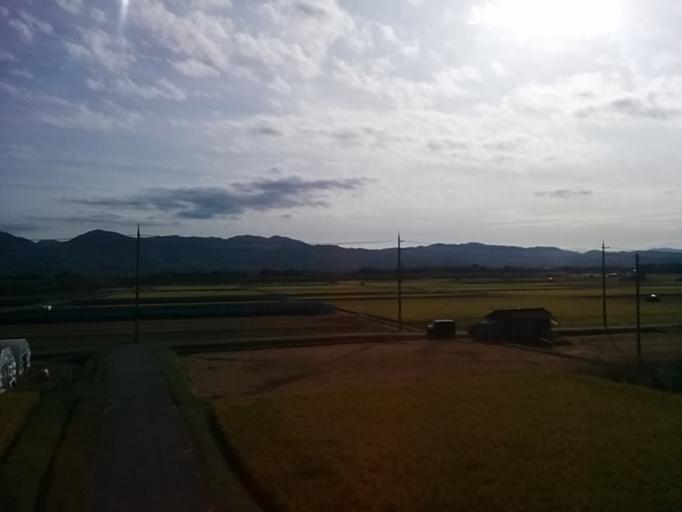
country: JP
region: Kyoto
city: Tanabe
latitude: 34.7934
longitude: 135.7874
